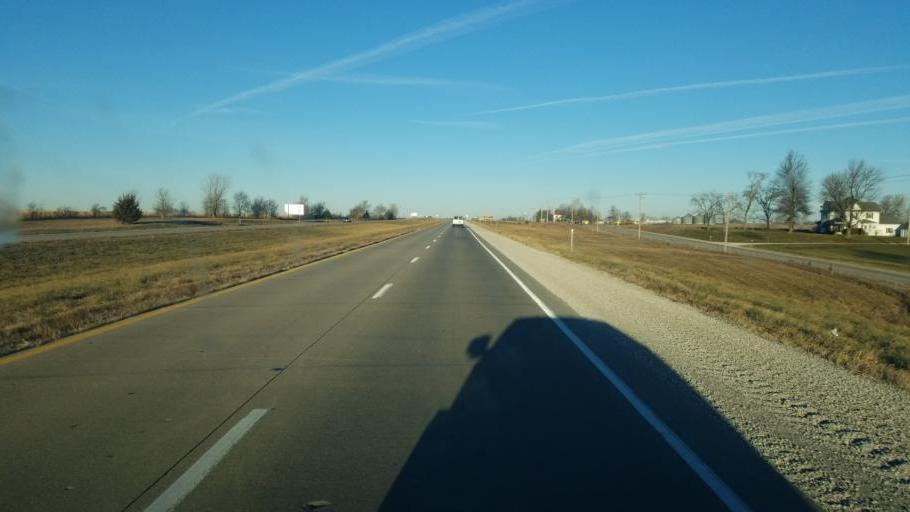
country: US
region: Iowa
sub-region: Mahaska County
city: Oskaloosa
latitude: 41.3116
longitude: -92.6828
